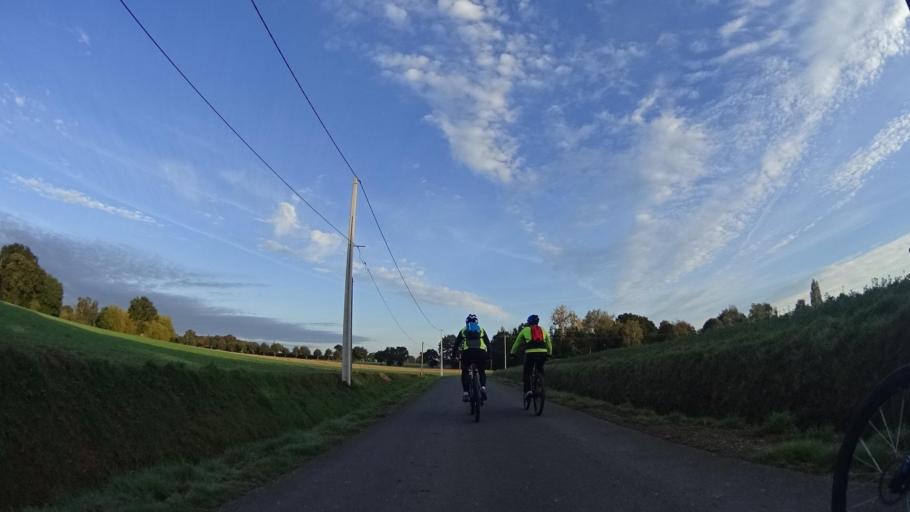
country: FR
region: Brittany
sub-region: Departement des Cotes-d'Armor
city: Evran
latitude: 48.3507
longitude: -1.9407
